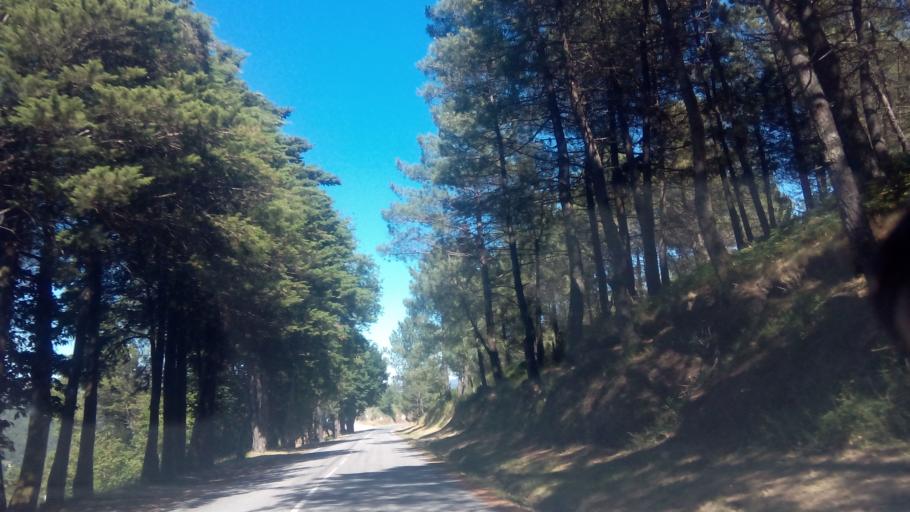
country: PT
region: Vila Real
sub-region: Santa Marta de Penaguiao
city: Santa Marta de Penaguiao
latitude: 41.2800
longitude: -7.8717
